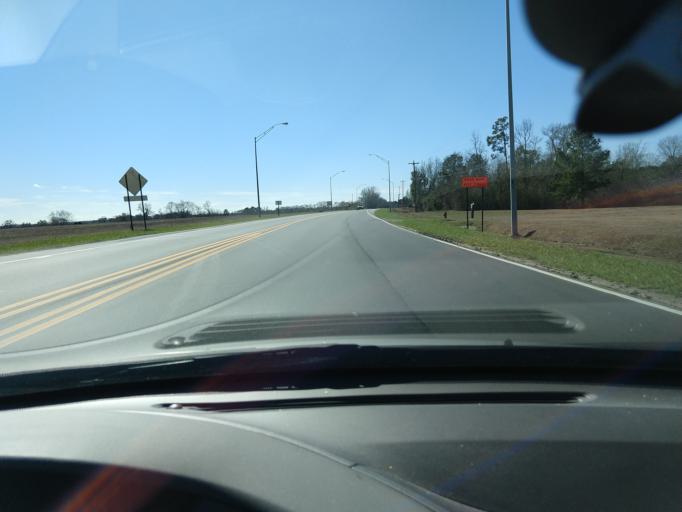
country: US
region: Alabama
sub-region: Covington County
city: Andalusia
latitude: 31.2770
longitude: -86.5065
